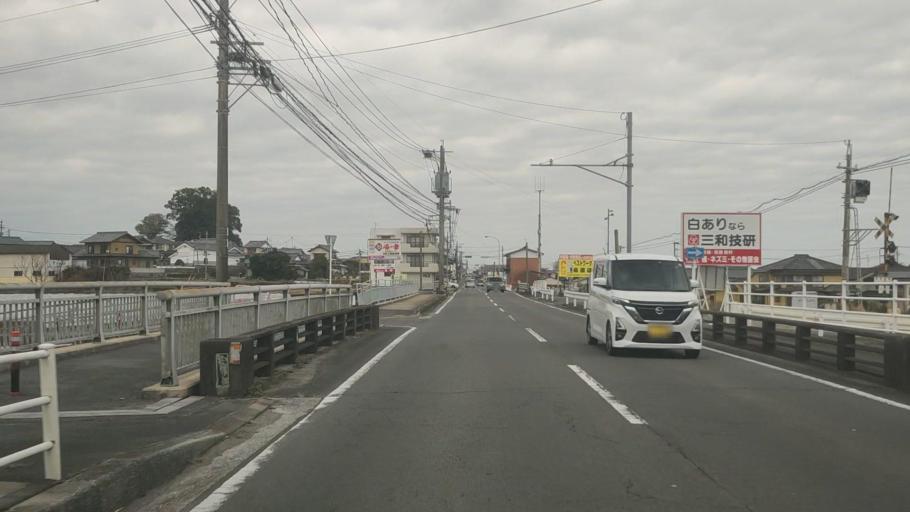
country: JP
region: Nagasaki
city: Shimabara
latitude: 32.8235
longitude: 130.3527
